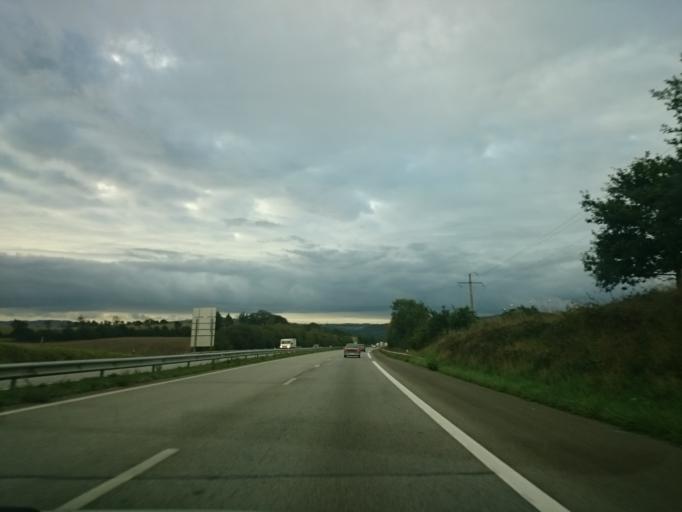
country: FR
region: Brittany
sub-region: Departement du Finistere
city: Chateaulin
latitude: 48.2020
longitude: -4.0441
